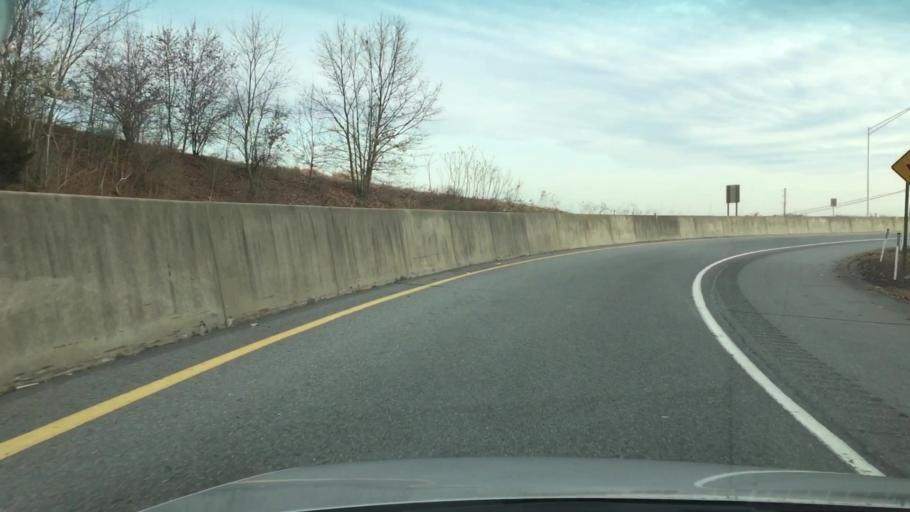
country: US
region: Pennsylvania
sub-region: Columbia County
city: Light Street
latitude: 41.0284
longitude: -76.4266
